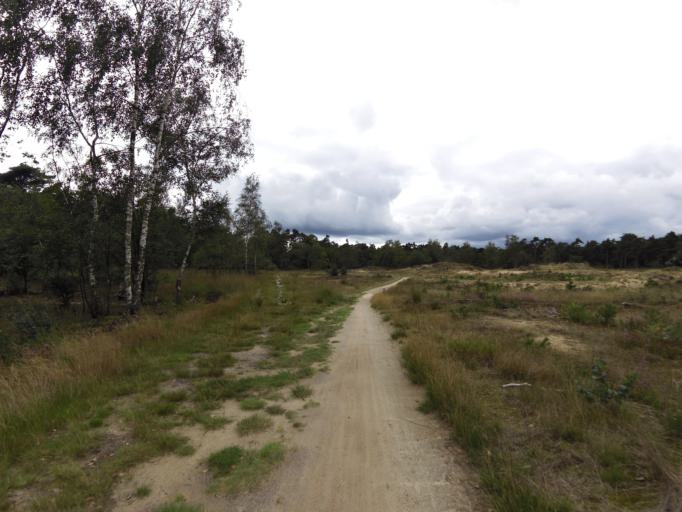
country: NL
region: North Brabant
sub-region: Gemeente Loon op Zand
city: Loon op Zand
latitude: 51.6497
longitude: 5.1459
